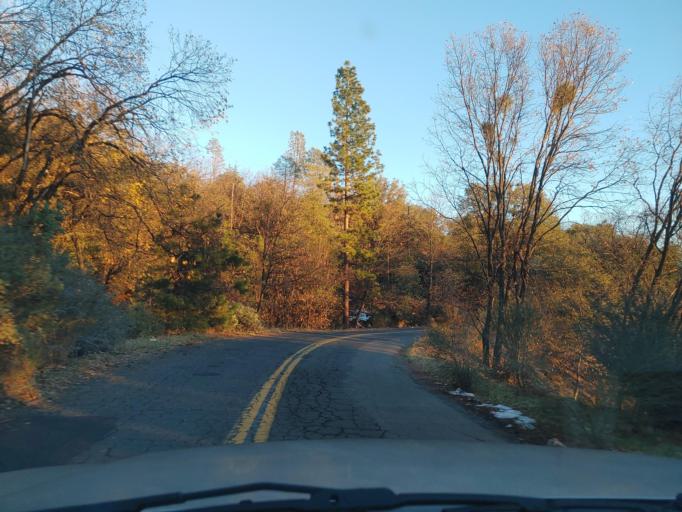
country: US
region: California
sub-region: Tuolumne County
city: Cedar Ridge
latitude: 38.0402
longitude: -120.2787
